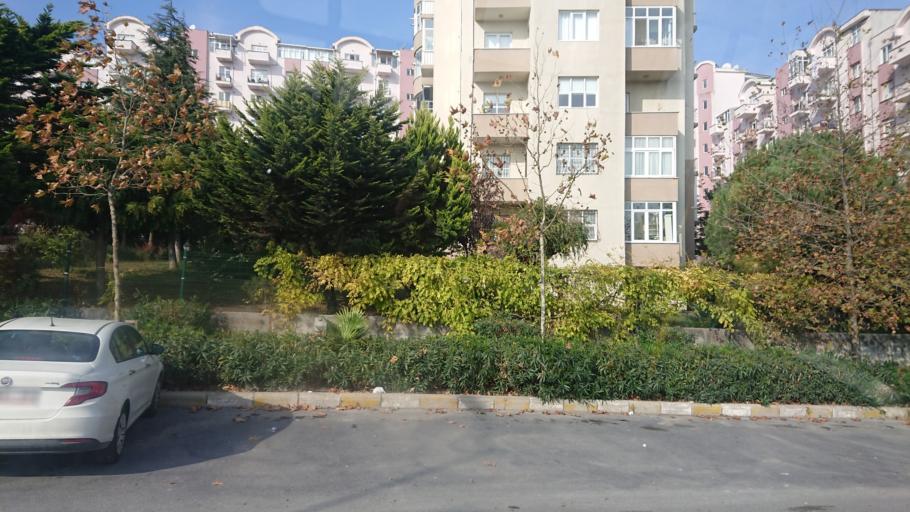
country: TR
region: Istanbul
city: Esenyurt
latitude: 41.0730
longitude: 28.6670
